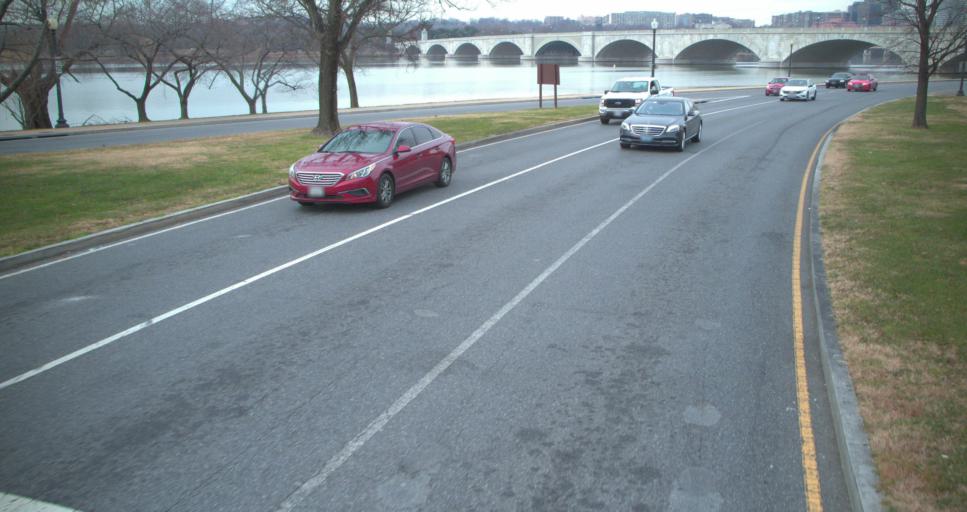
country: US
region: Washington, D.C.
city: Washington, D.C.
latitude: 38.8863
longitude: -77.0514
